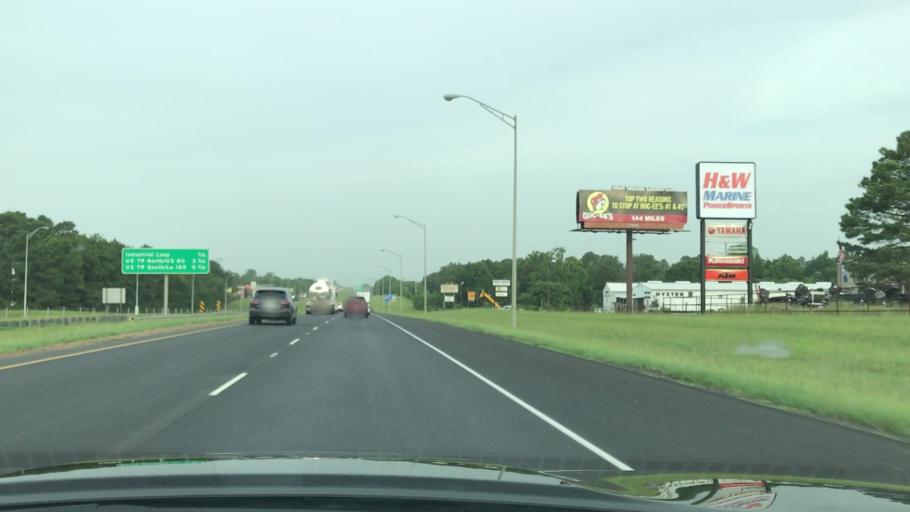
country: US
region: Louisiana
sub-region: Caddo Parish
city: Greenwood
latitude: 32.4496
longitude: -93.8844
